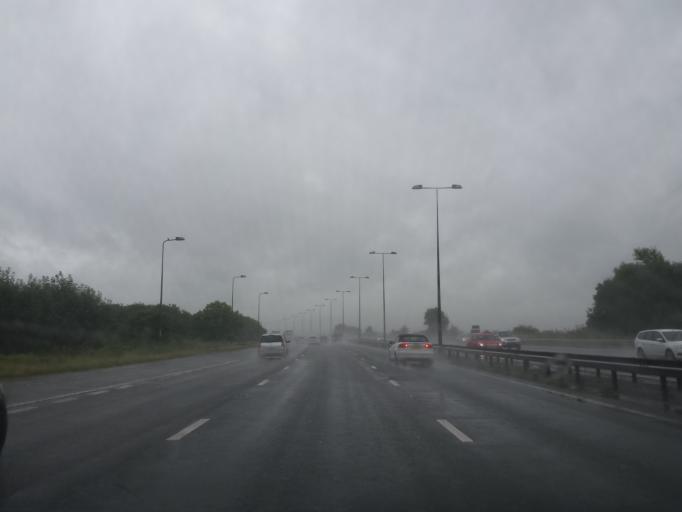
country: GB
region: England
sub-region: Derbyshire
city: Long Eaton
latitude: 52.9098
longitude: -1.3002
